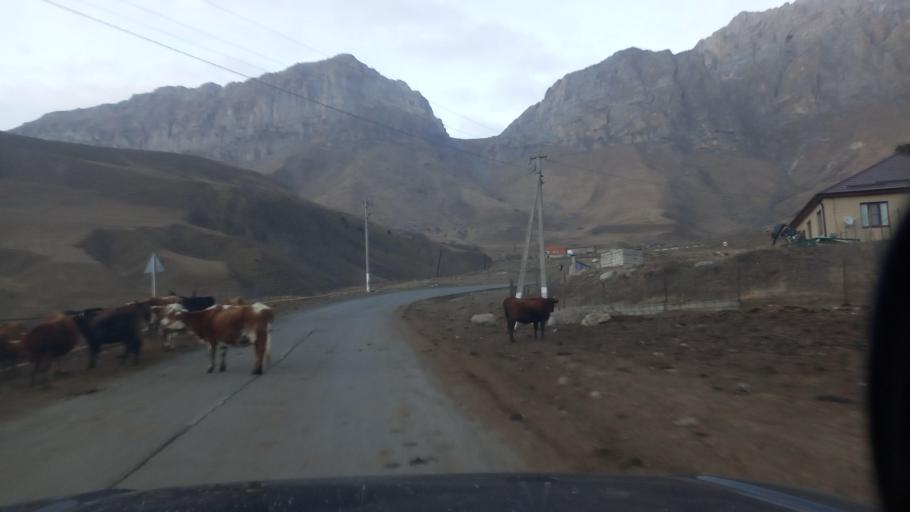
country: RU
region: Ingushetiya
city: Dzhayrakh
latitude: 42.8165
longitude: 44.8145
